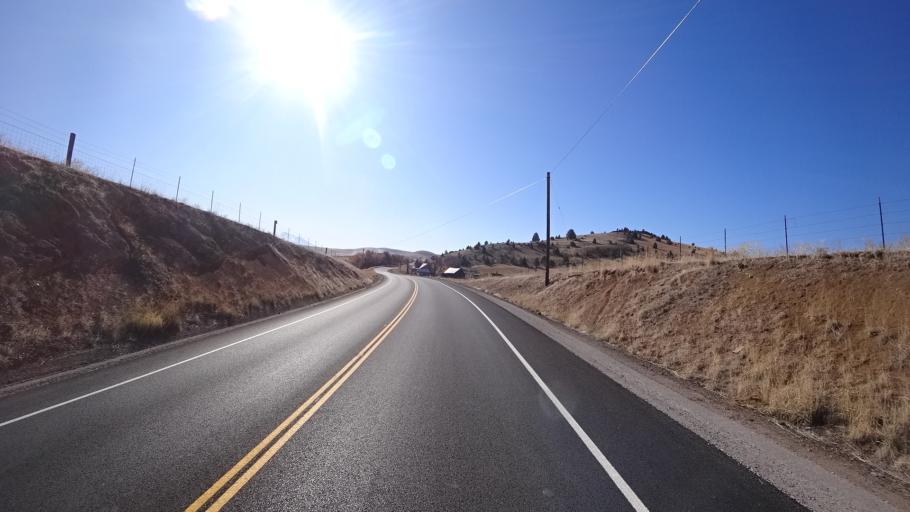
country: US
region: California
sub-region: Siskiyou County
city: Montague
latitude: 41.8564
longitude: -122.4656
